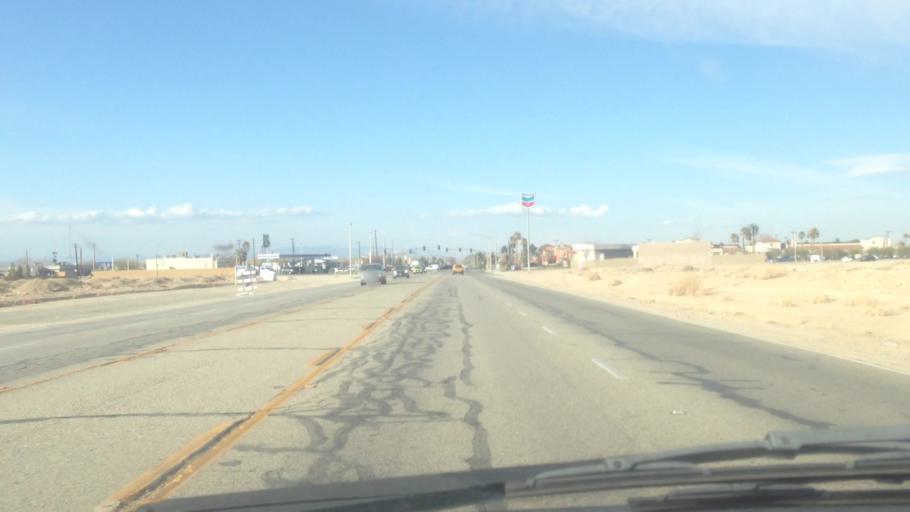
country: US
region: California
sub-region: Los Angeles County
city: Lancaster
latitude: 34.7013
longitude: -118.1659
